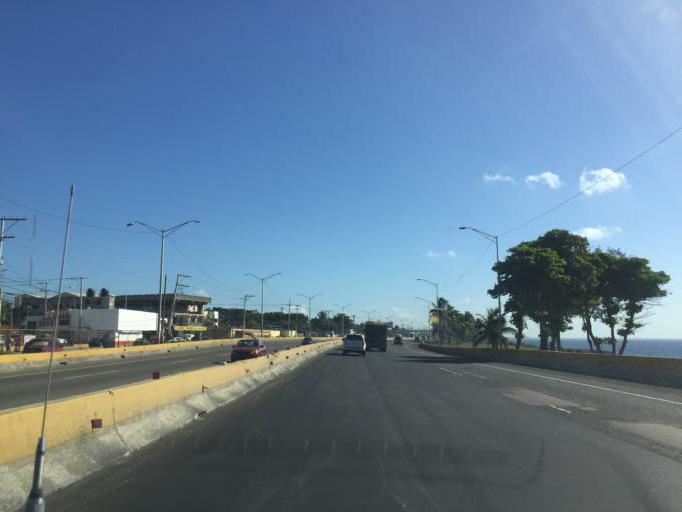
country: DO
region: Santo Domingo
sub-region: Santo Domingo
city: Santo Domingo Este
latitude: 18.4646
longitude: -69.8078
